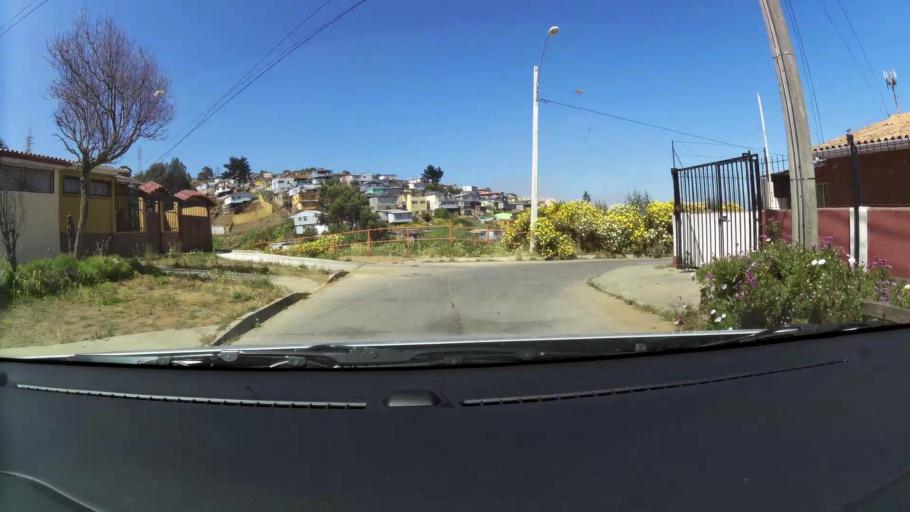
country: CL
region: Valparaiso
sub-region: Provincia de Valparaiso
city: Valparaiso
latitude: -33.0418
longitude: -71.6497
